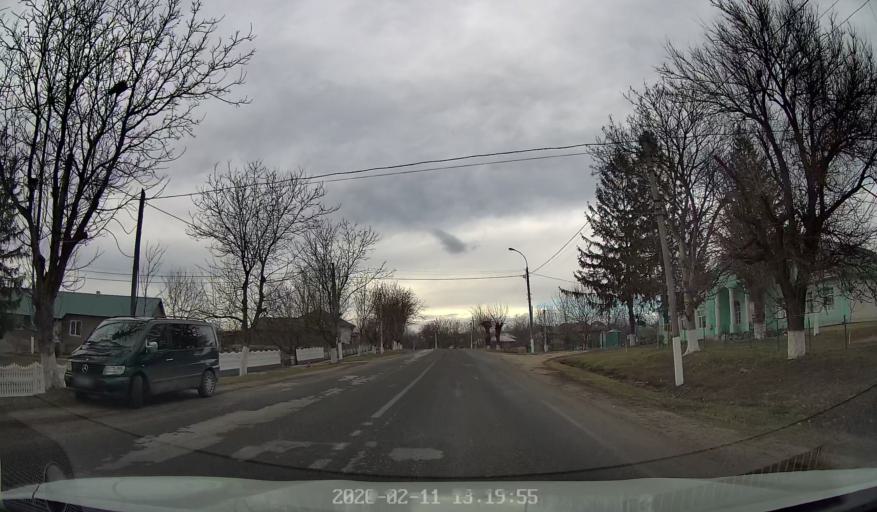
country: RO
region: Botosani
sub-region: Comuna Radauti-Prut
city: Rediu
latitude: 48.2697
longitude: 26.7206
